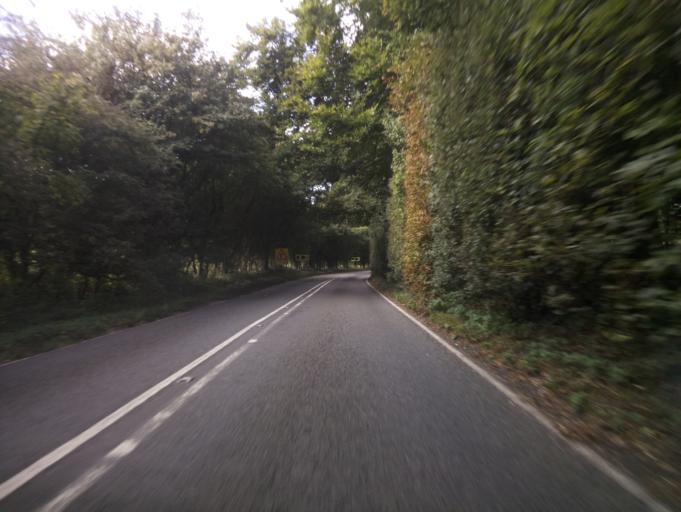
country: GB
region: England
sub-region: Hampshire
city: Basingstoke
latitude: 51.2244
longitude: -1.0651
